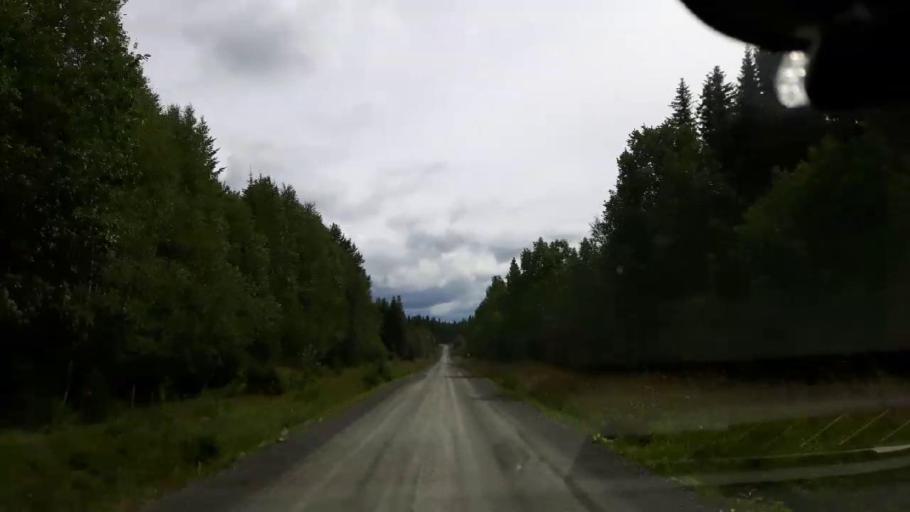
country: SE
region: Jaemtland
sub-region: Krokoms Kommun
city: Valla
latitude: 63.6444
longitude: 13.9911
